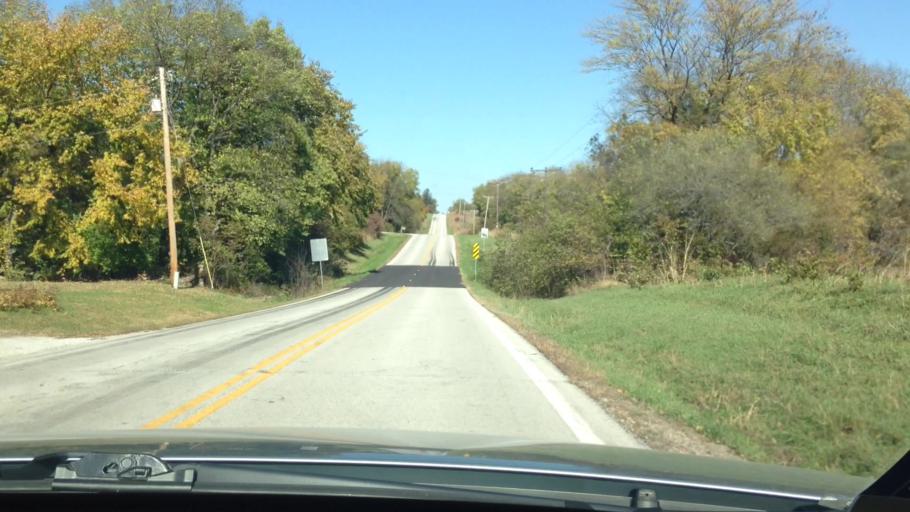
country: US
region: Missouri
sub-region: Platte County
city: Weatherby Lake
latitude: 39.3178
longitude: -94.6489
